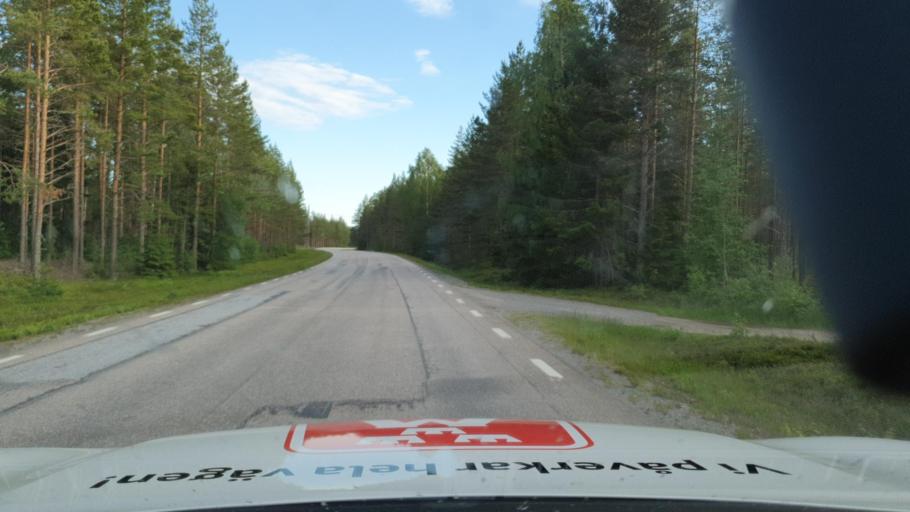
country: SE
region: Vaesterbotten
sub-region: Umea Kommun
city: Roback
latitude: 63.8642
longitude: 20.1449
